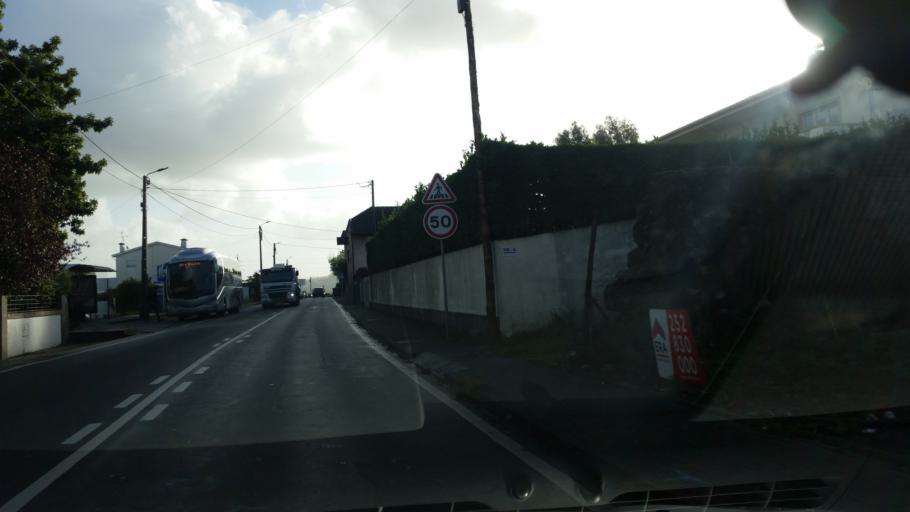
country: PT
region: Porto
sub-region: Santo Tirso
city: Aves
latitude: 41.3584
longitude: -8.4413
